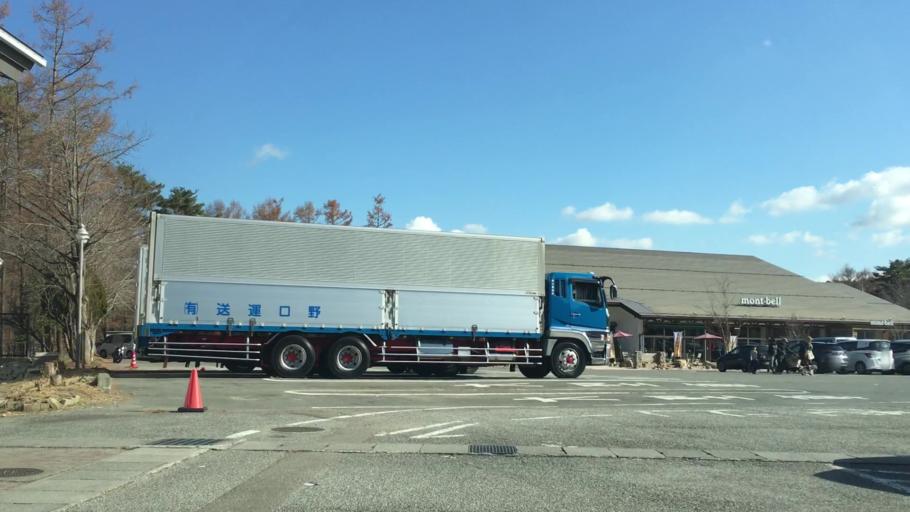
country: JP
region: Yamanashi
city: Fujikawaguchiko
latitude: 35.4593
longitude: 138.8026
